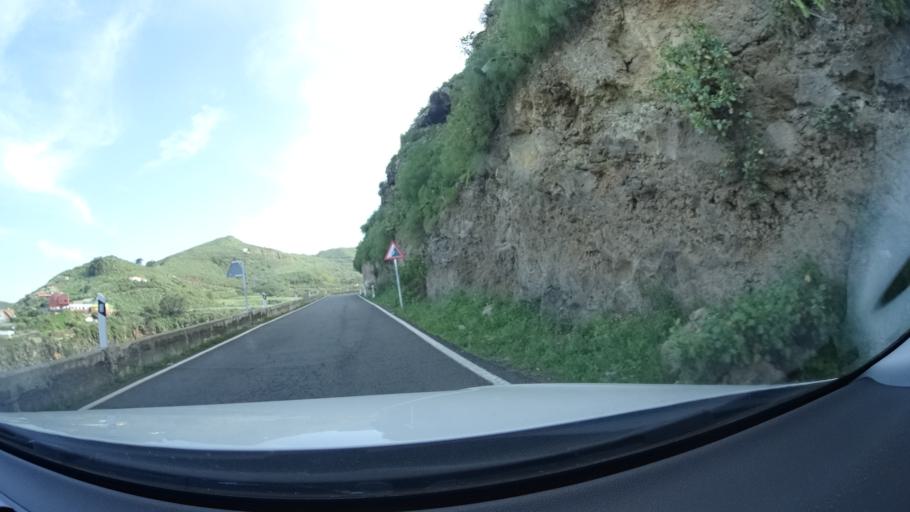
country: ES
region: Canary Islands
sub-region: Provincia de Las Palmas
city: Guia
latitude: 28.1139
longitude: -15.6415
